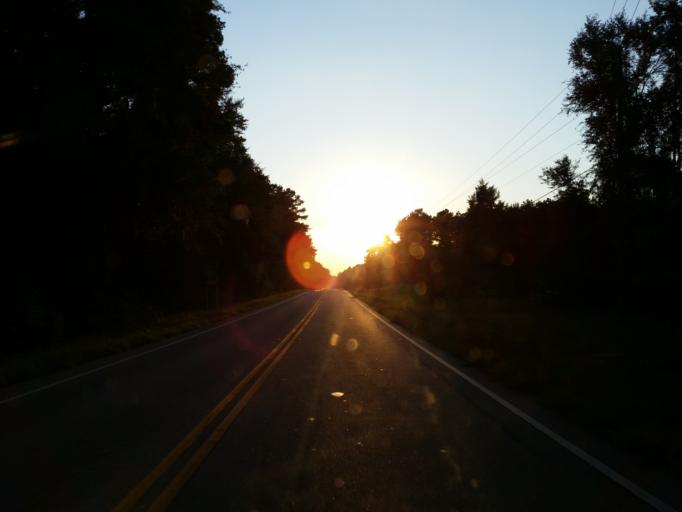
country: US
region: Georgia
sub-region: Berrien County
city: Nashville
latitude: 31.2142
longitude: -83.2650
